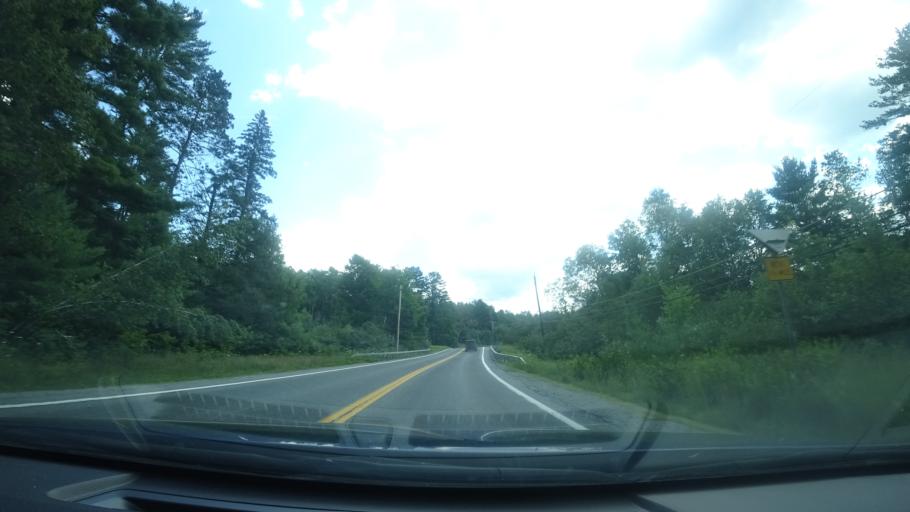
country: US
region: New York
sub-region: Warren County
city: Warrensburg
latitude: 43.6608
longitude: -73.8191
